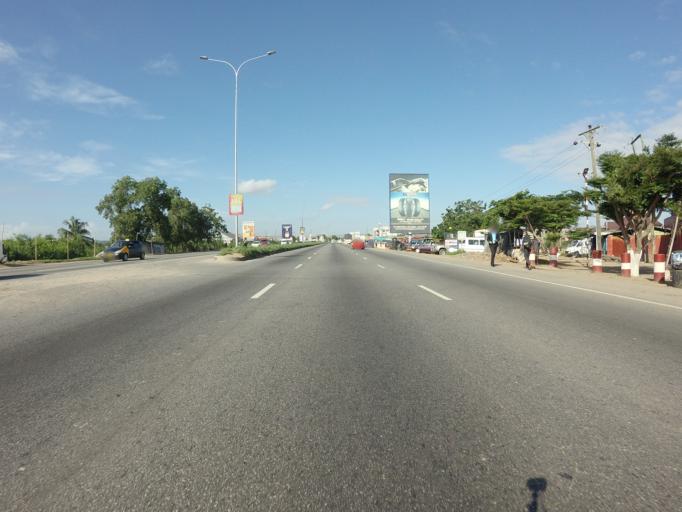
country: GH
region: Greater Accra
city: Gbawe
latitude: 5.5554
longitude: -0.3050
